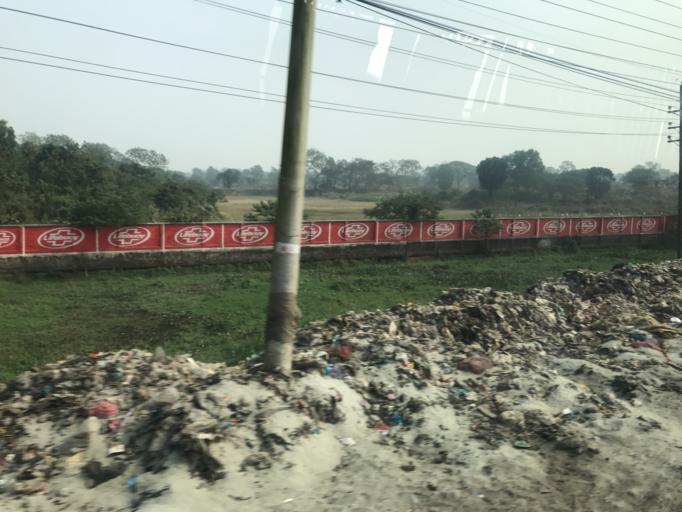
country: BD
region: Dhaka
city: Tungi
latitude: 23.8936
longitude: 90.2717
